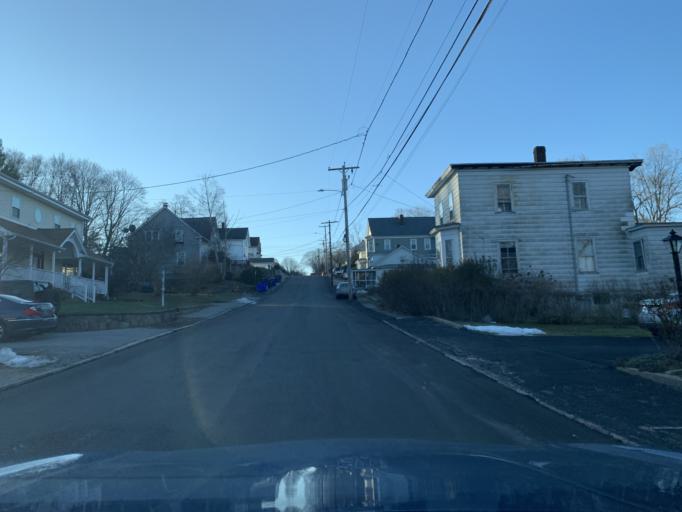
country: US
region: Rhode Island
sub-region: Kent County
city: West Warwick
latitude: 41.7123
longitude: -71.5254
